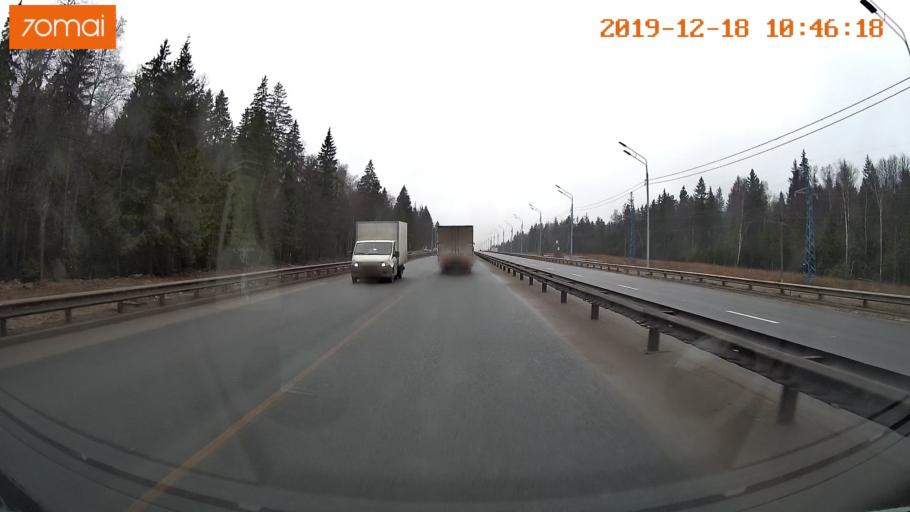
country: RU
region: Moskovskaya
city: Aprelevka
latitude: 55.4832
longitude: 37.0500
